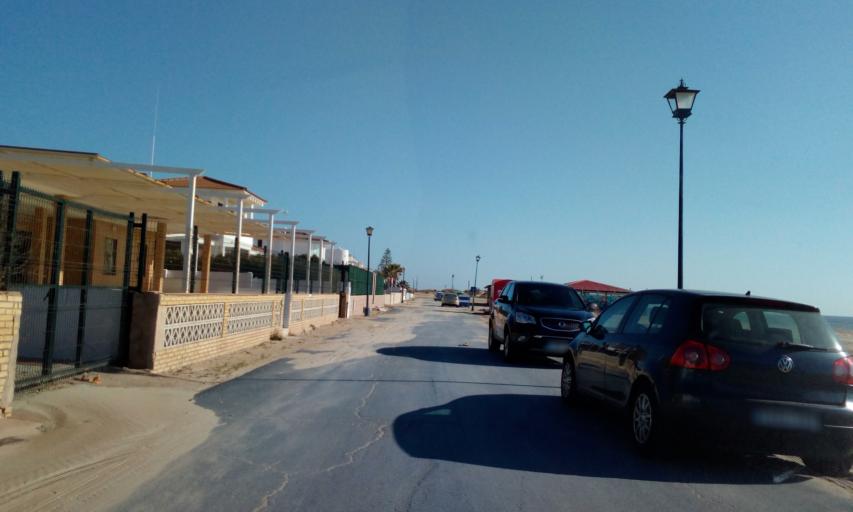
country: ES
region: Andalusia
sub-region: Provincia de Huelva
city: Lepe
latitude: 37.2063
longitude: -7.1998
